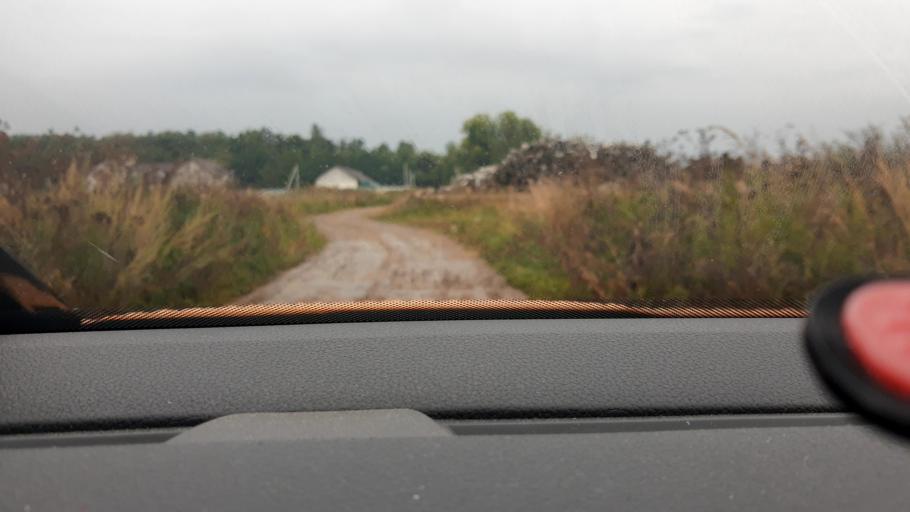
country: RU
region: Moskovskaya
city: Obukhovo
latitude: 55.8083
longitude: 38.2789
